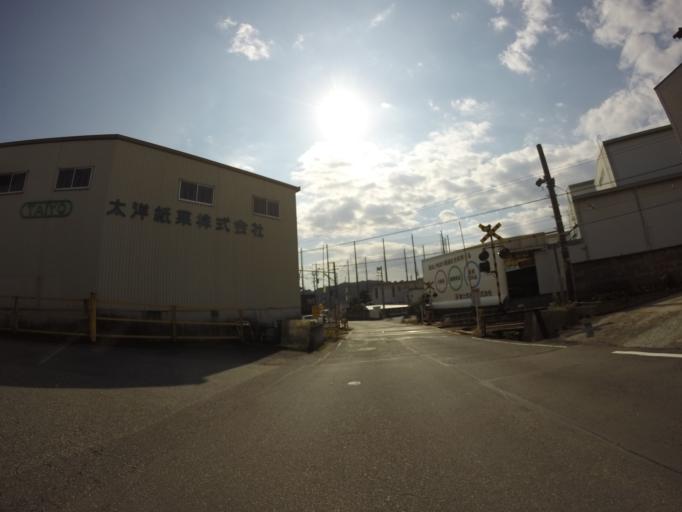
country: JP
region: Shizuoka
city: Fujinomiya
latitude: 35.2080
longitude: 138.6337
